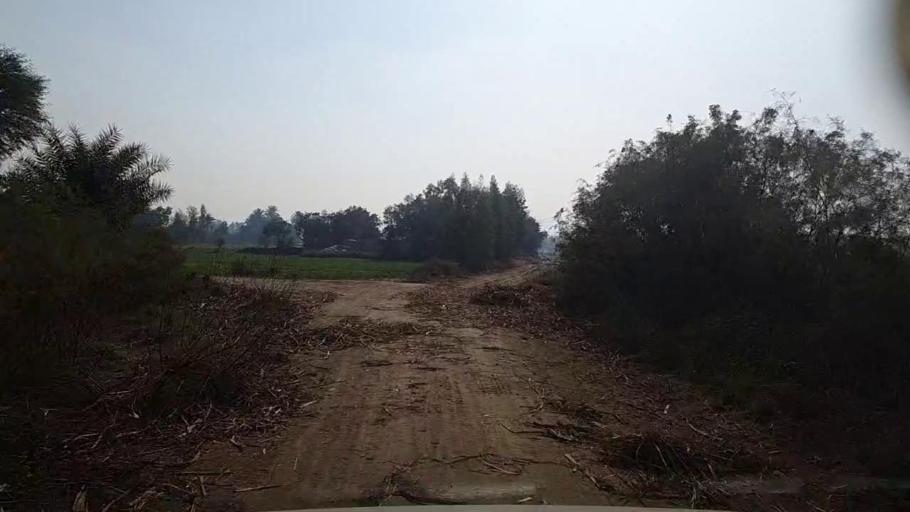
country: PK
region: Sindh
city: Mirpur Mathelo
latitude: 27.9239
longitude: 69.6561
